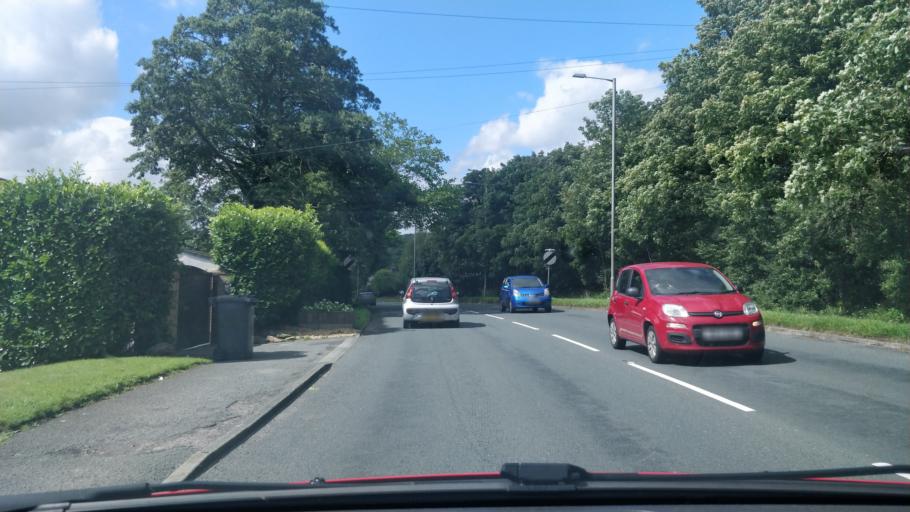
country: GB
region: England
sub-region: Lancashire
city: Appley Bridge
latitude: 53.5930
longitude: -2.7294
